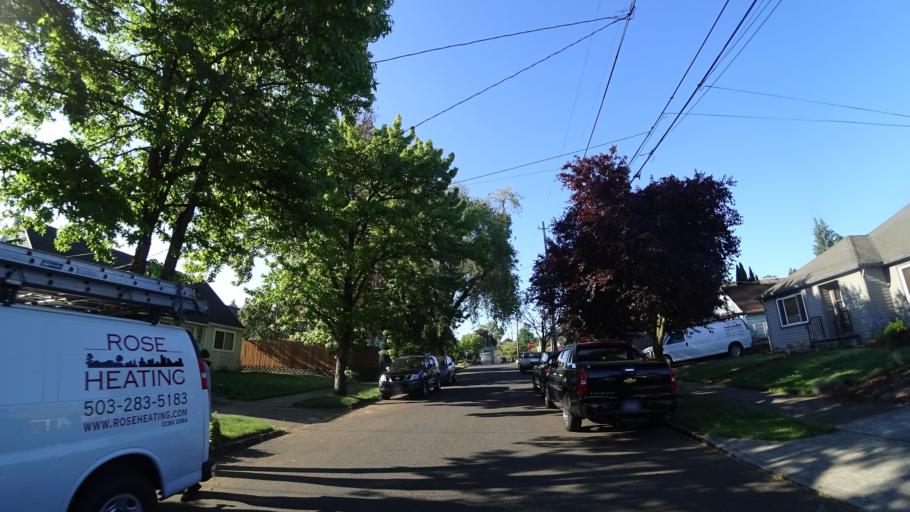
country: US
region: Oregon
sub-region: Multnomah County
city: Portland
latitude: 45.5669
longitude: -122.6471
